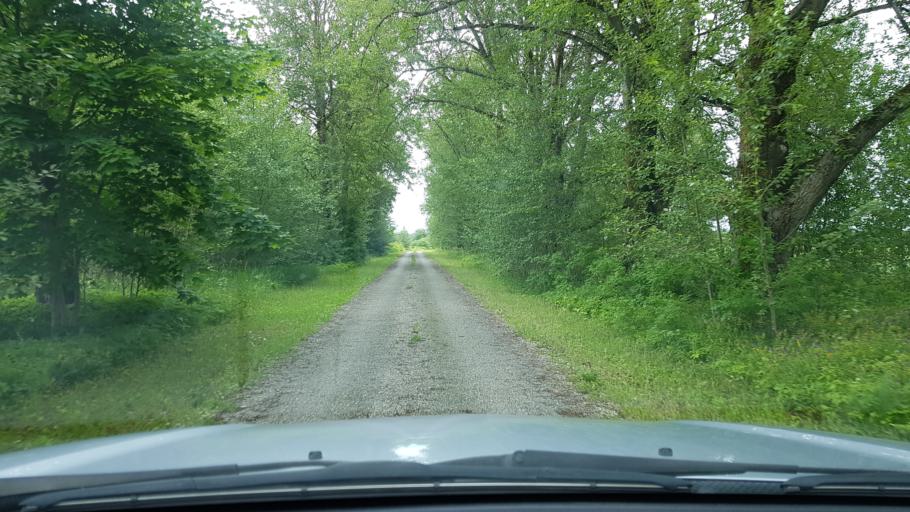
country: EE
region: Ida-Virumaa
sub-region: Narva-Joesuu linn
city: Narva-Joesuu
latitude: 59.3422
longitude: 27.9419
